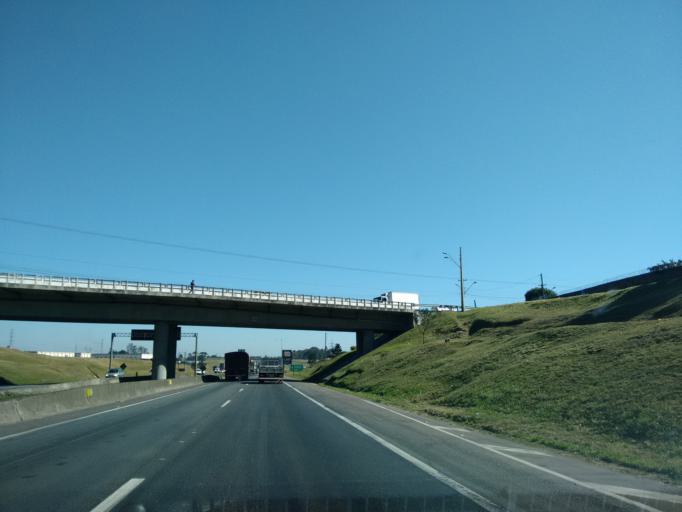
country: BR
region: Parana
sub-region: Sao Jose Dos Pinhais
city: Sao Jose dos Pinhais
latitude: -25.5462
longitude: -49.2932
